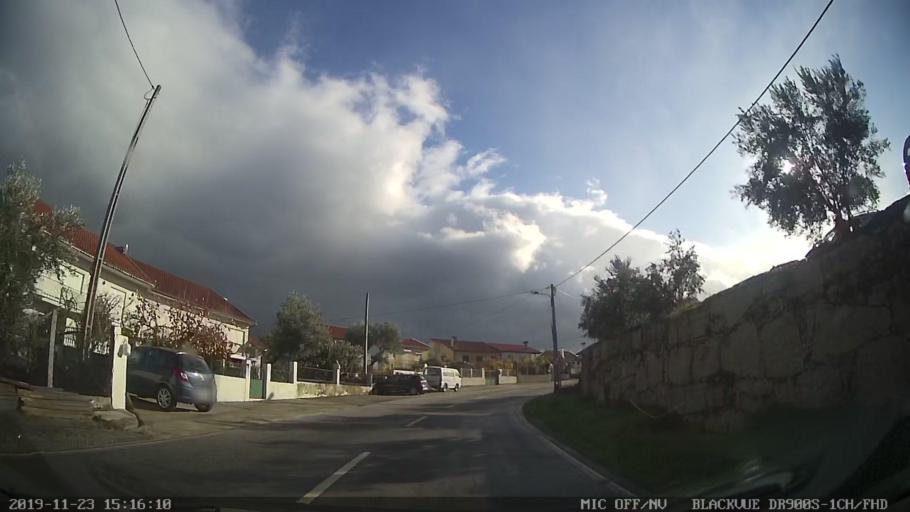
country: PT
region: Vila Real
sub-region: Peso da Regua
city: Peso da Regua
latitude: 41.1283
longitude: -7.7840
